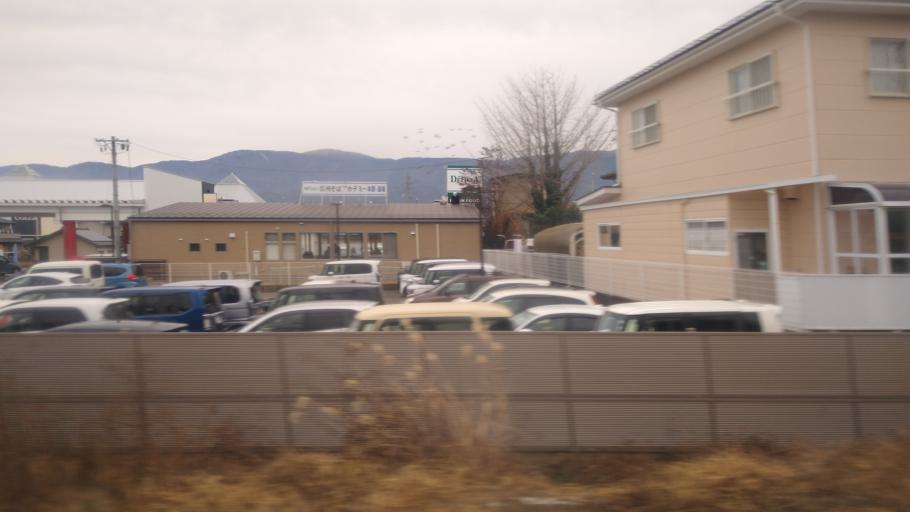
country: JP
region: Nagano
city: Shiojiri
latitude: 36.1495
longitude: 137.9497
